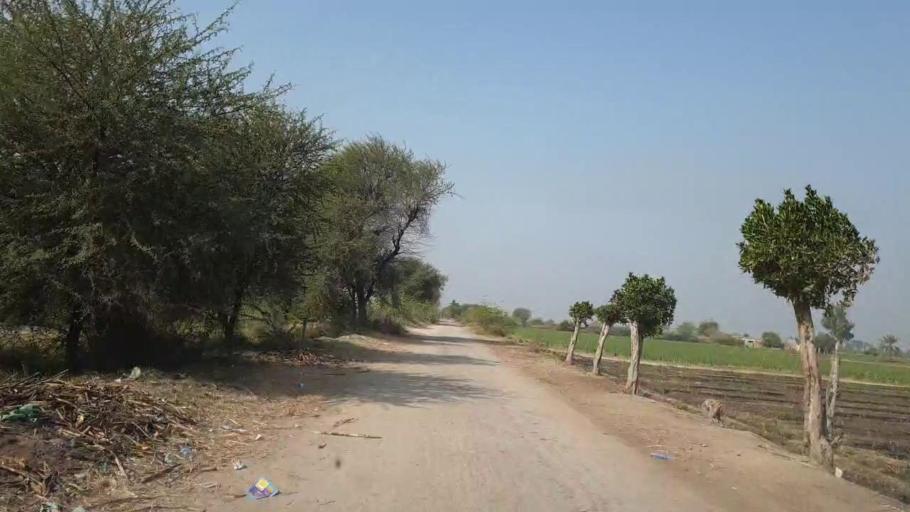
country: PK
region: Sindh
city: Mirpur Khas
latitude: 25.5819
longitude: 69.0107
